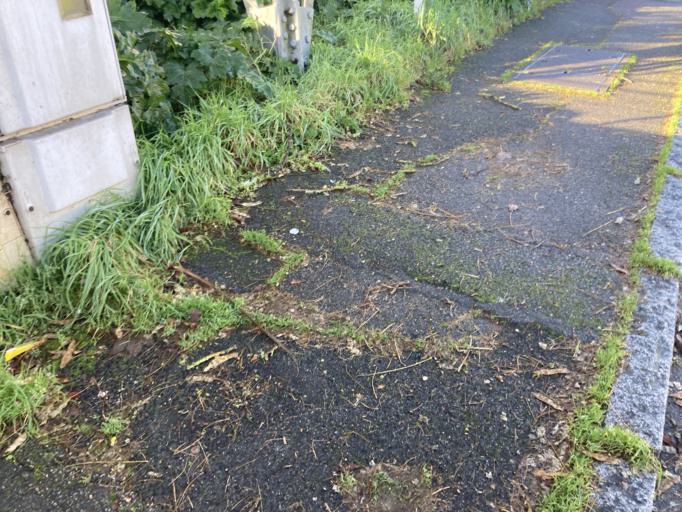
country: FR
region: Pays de la Loire
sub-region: Departement de la Loire-Atlantique
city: Saint-Sebastien-sur-Loire
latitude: 47.2039
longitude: -1.4917
